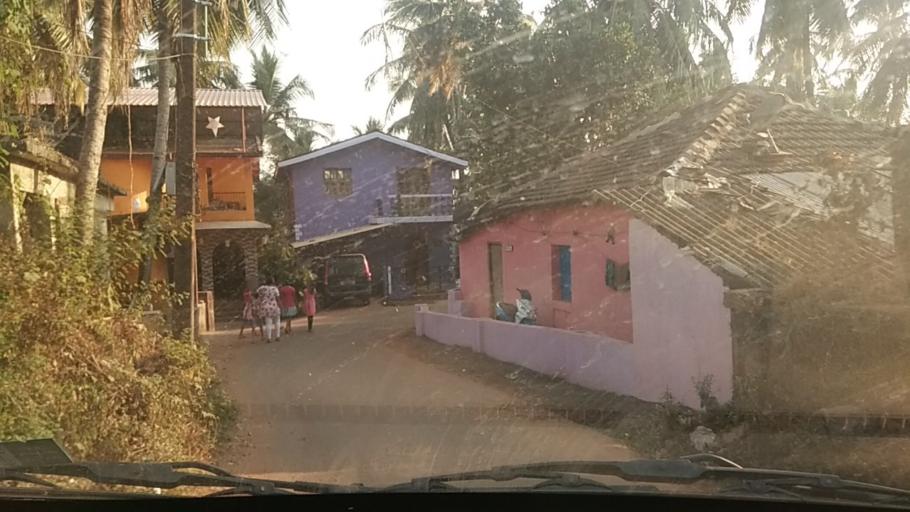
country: IN
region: Goa
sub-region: North Goa
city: Goa Velha
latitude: 15.4607
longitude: 73.8803
